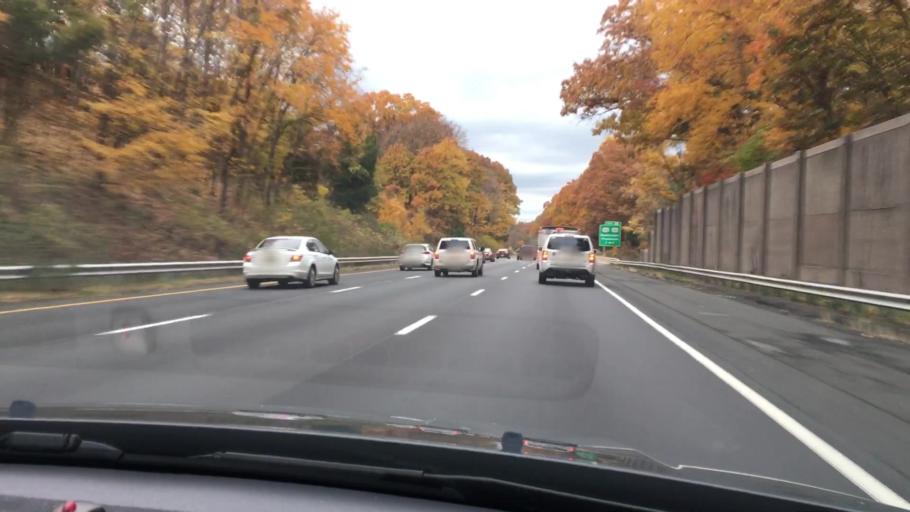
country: US
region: New Jersey
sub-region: Somerset County
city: Bedminster
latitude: 40.6714
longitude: -74.6232
